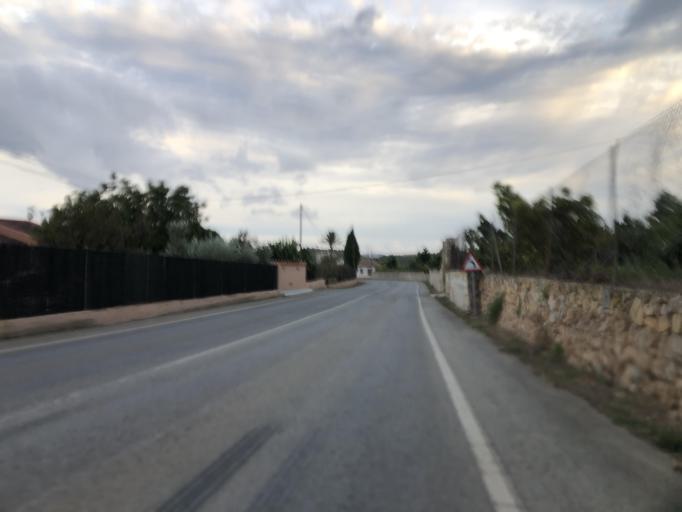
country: ES
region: Valencia
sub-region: Provincia de Alicante
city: Polop
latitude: 38.6283
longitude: -0.1407
